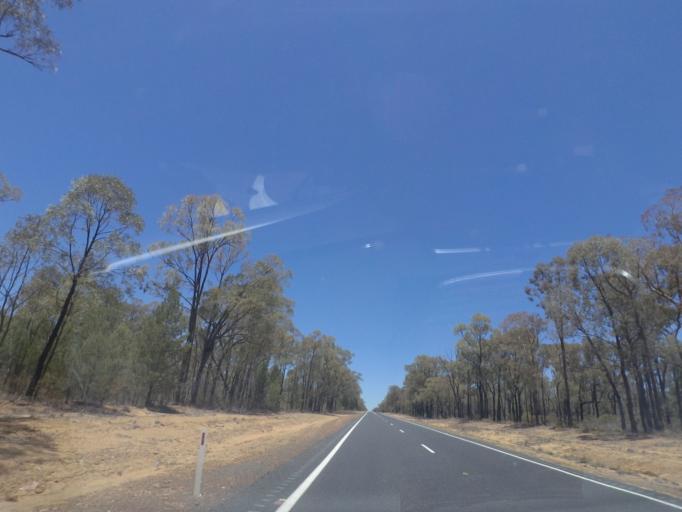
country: AU
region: New South Wales
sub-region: Narrabri
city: Narrabri
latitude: -30.7330
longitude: 149.5195
